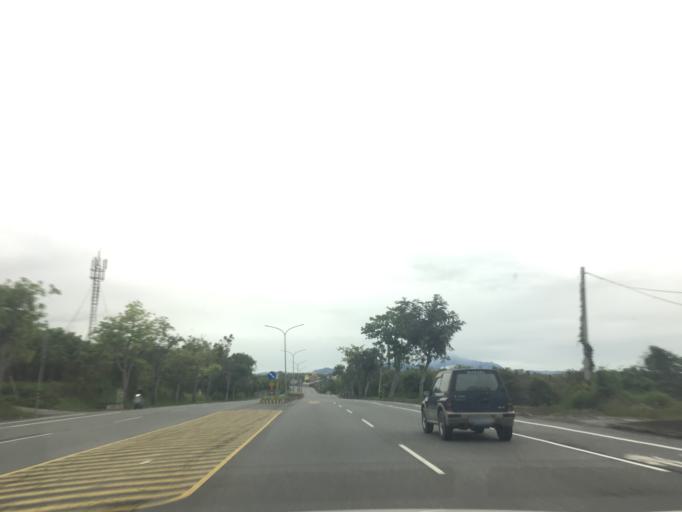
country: TW
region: Taiwan
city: Taitung City
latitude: 22.7218
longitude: 121.0542
